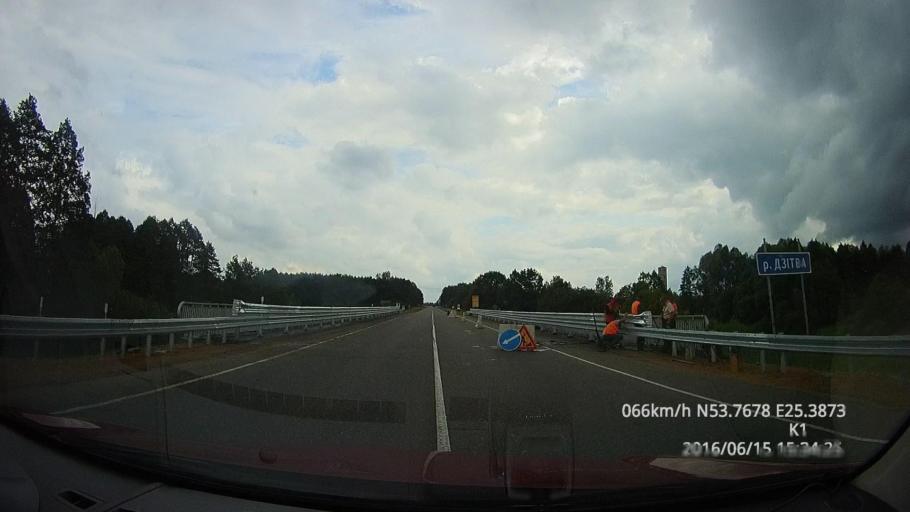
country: BY
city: Berezovka
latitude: 53.7672
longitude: 25.3876
